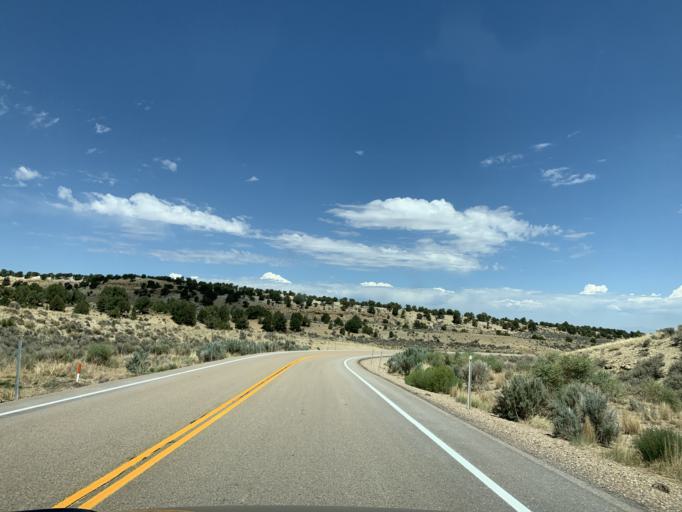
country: US
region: Utah
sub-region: Duchesne County
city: Duchesne
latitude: 39.8938
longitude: -110.2397
